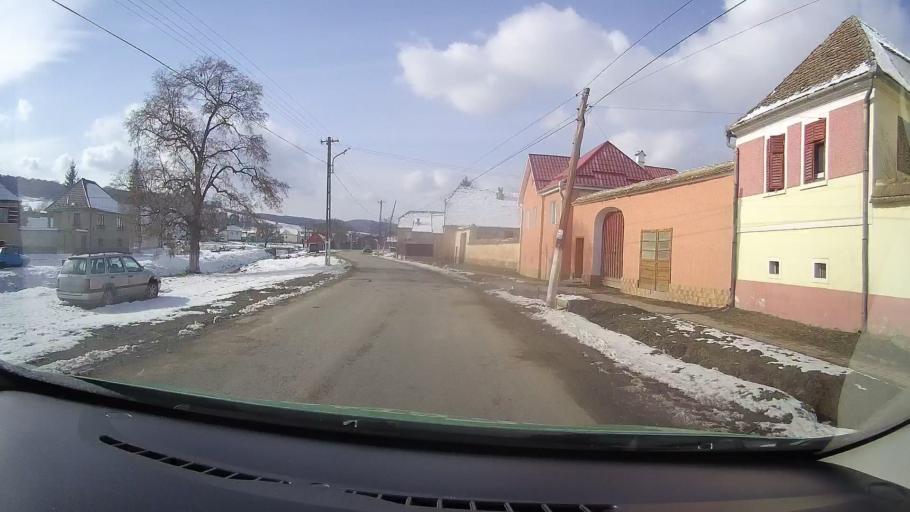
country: RO
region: Sibiu
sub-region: Comuna Iacobeni
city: Iacobeni
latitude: 46.0502
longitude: 24.7187
